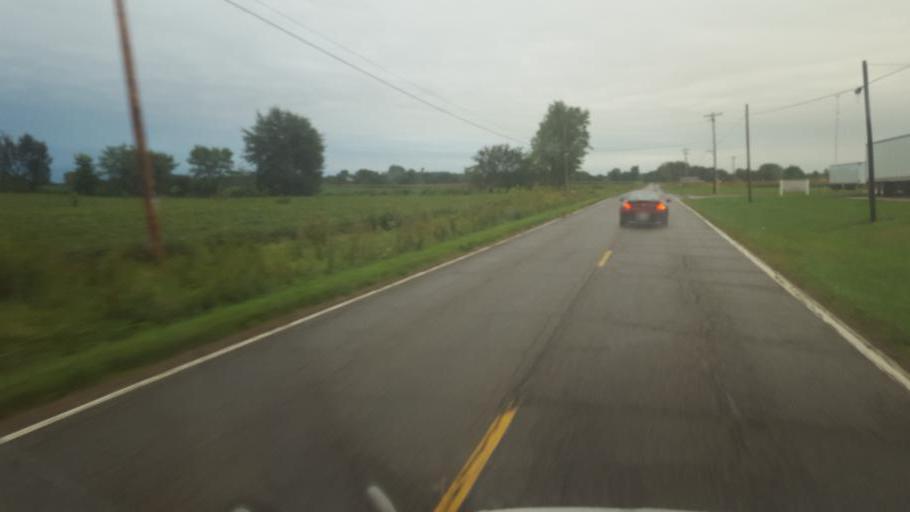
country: US
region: Ohio
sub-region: Licking County
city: Johnstown
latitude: 40.1877
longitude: -82.6924
